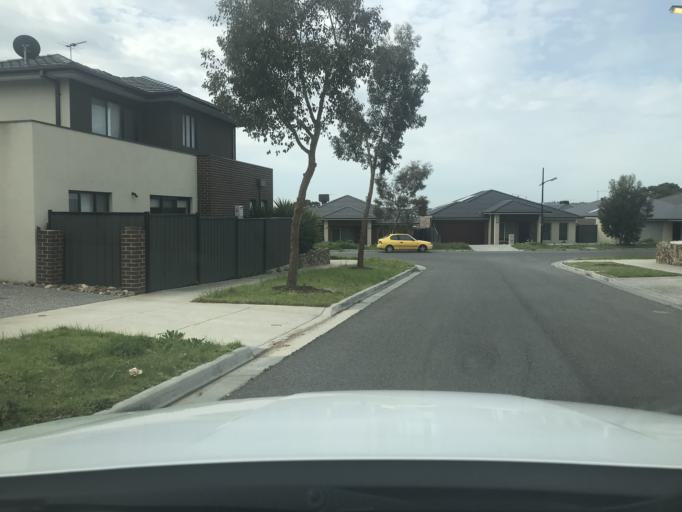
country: AU
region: Victoria
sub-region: Hume
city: Roxburgh Park
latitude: -37.5982
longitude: 144.8975
